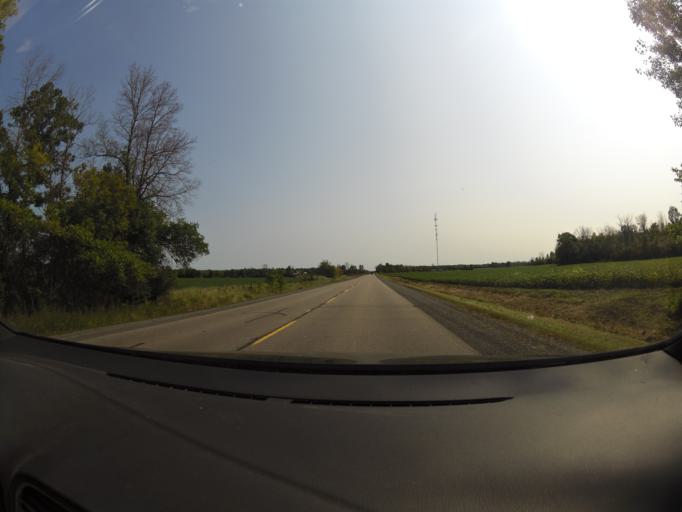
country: CA
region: Ontario
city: Arnprior
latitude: 45.4224
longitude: -76.1574
